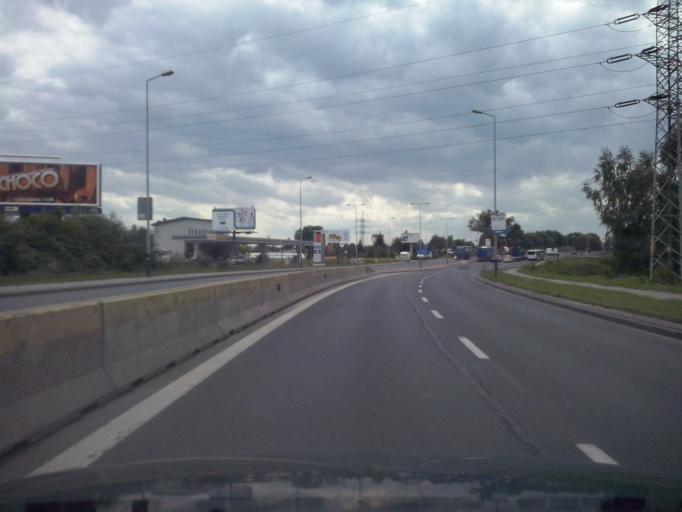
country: PL
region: Lesser Poland Voivodeship
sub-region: Krakow
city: Krakow
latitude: 50.0587
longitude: 20.0030
